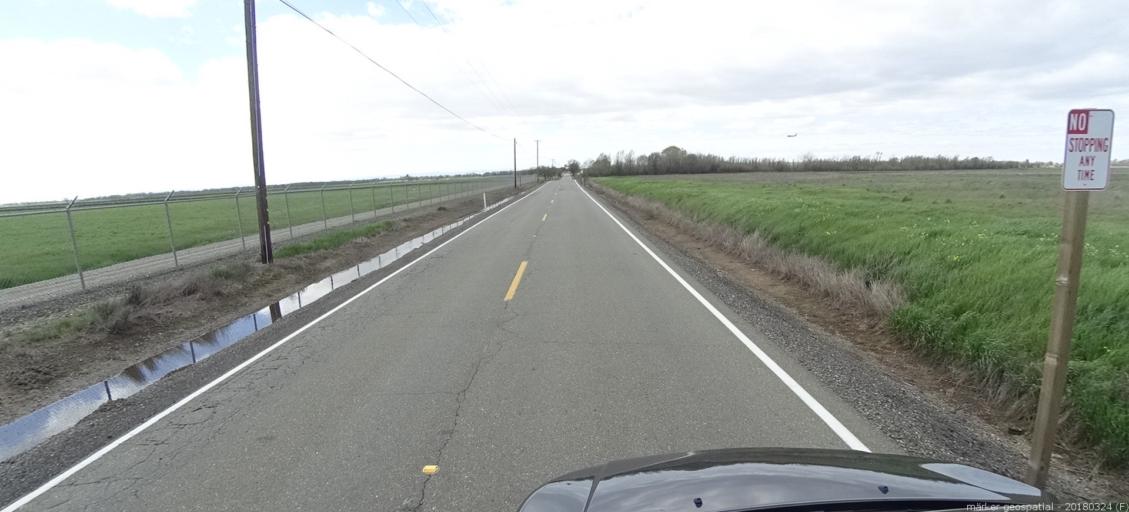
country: US
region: California
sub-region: Sacramento County
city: Elverta
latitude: 38.7144
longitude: -121.5810
